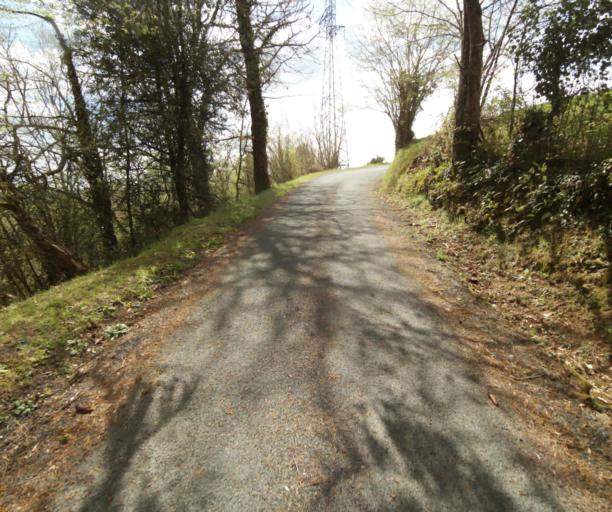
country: FR
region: Limousin
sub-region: Departement de la Correze
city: Sainte-Fortunade
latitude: 45.1889
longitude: 1.8637
